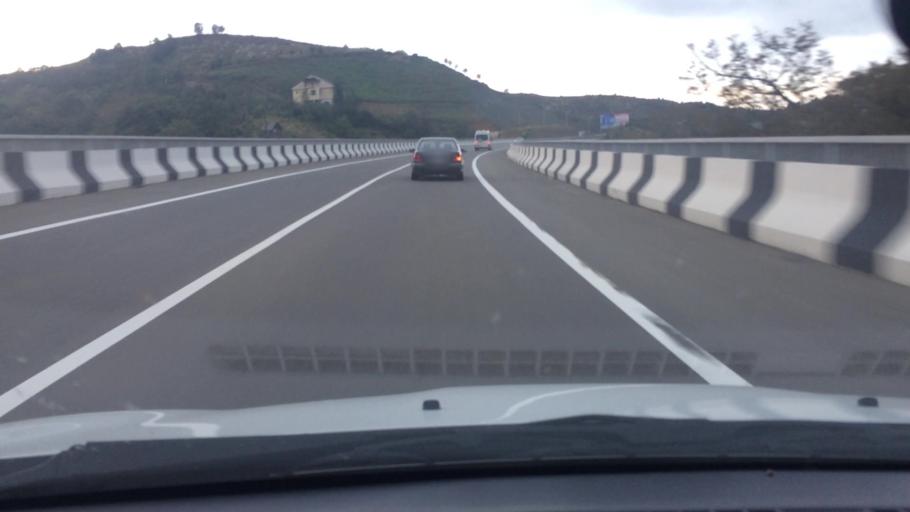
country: GE
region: Ajaria
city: Makhinjauri
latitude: 41.7216
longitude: 41.7496
